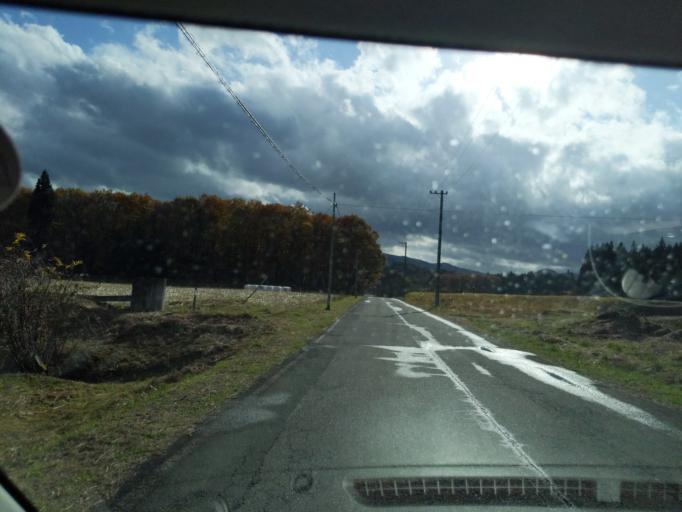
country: JP
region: Iwate
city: Mizusawa
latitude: 39.1100
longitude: 140.9729
